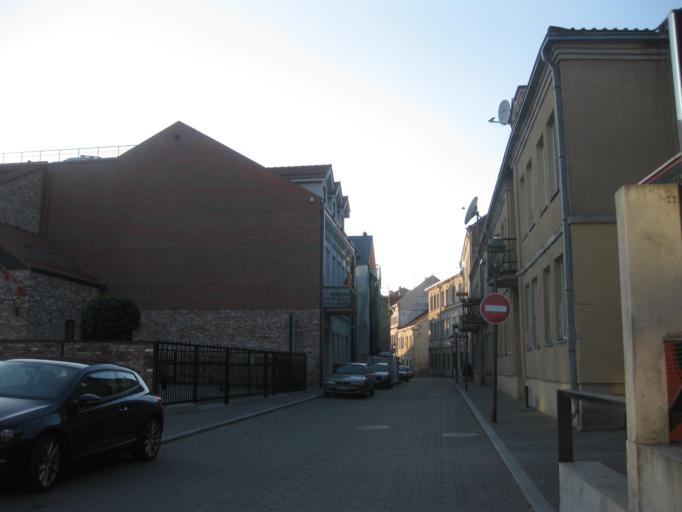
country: LT
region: Kauno apskritis
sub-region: Kaunas
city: Kaunas
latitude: 54.8959
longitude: 23.8958
